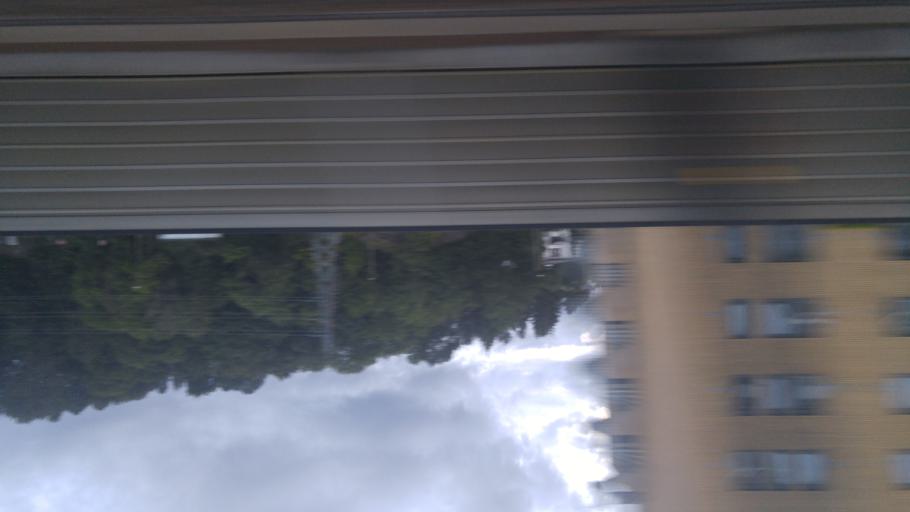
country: NO
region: Akershus
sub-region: Skedsmo
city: Lillestrom
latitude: 59.9649
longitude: 11.0661
